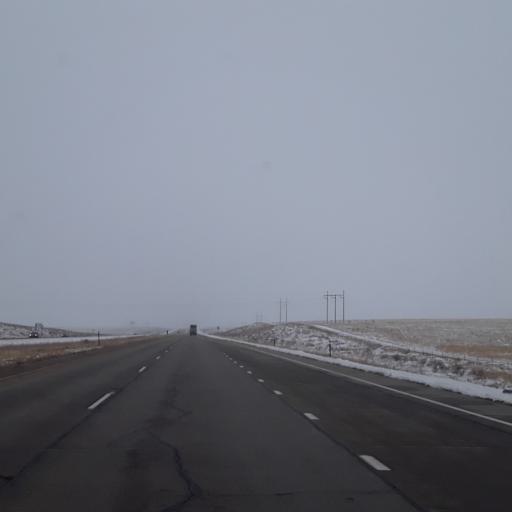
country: US
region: Colorado
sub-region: Logan County
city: Sterling
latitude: 40.7108
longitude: -103.0511
